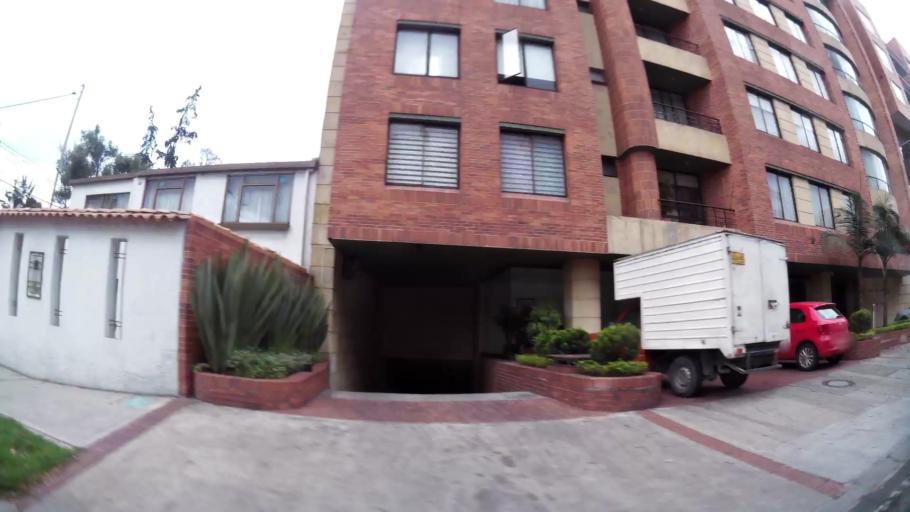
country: CO
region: Bogota D.C.
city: Barrio San Luis
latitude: 4.6970
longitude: -74.0625
